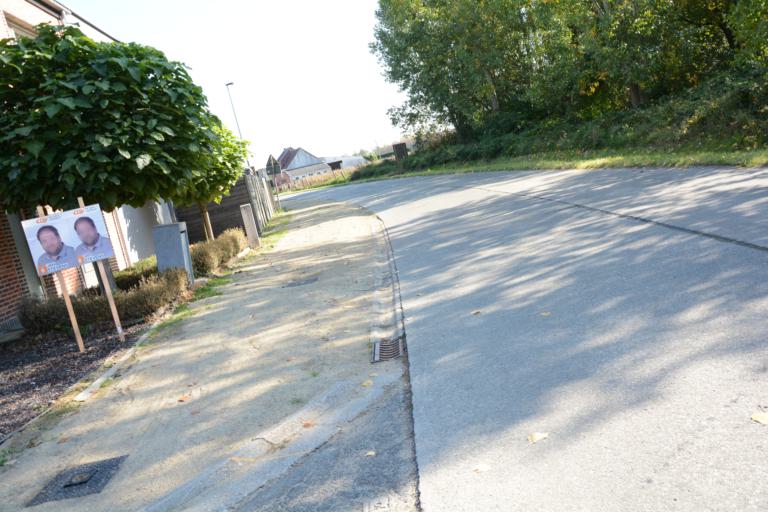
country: BE
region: Flanders
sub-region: Provincie Oost-Vlaanderen
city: Buggenhout
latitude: 51.0216
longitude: 4.2282
